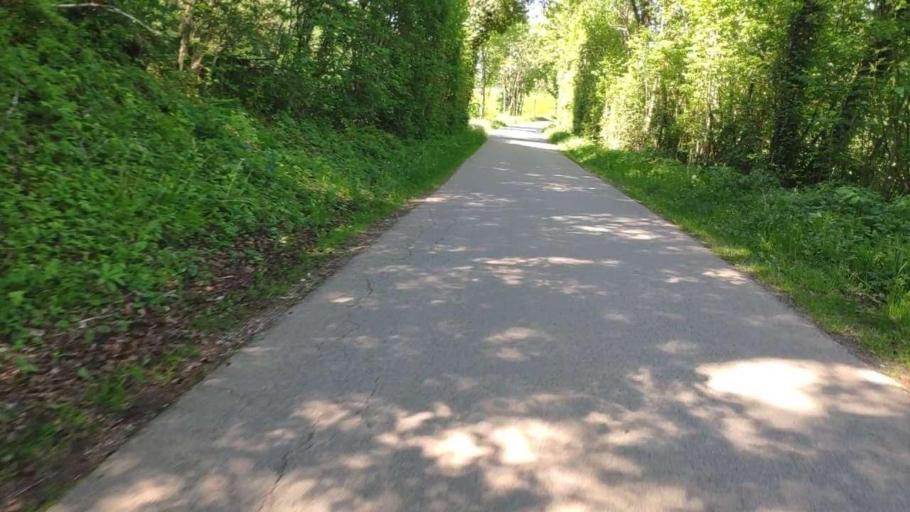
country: FR
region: Franche-Comte
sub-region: Departement du Jura
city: Poligny
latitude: 46.7378
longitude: 5.7673
